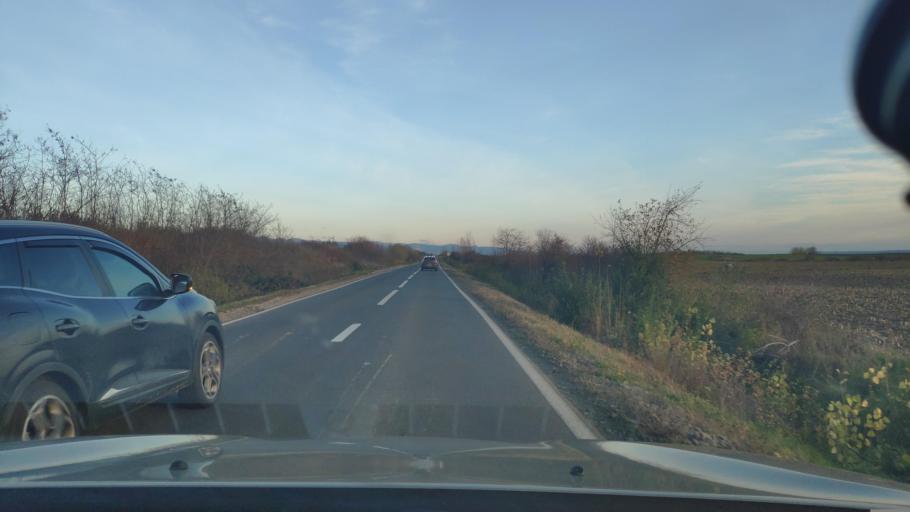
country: RO
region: Satu Mare
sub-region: Comuna Mediesu Aurit
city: Mediesu Aurit
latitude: 47.7700
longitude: 23.1463
